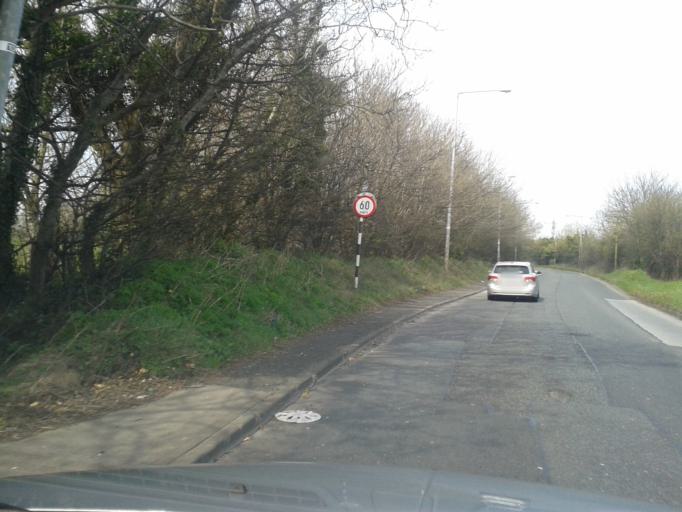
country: IE
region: Leinster
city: Ballymun
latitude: 53.4137
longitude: -6.2655
